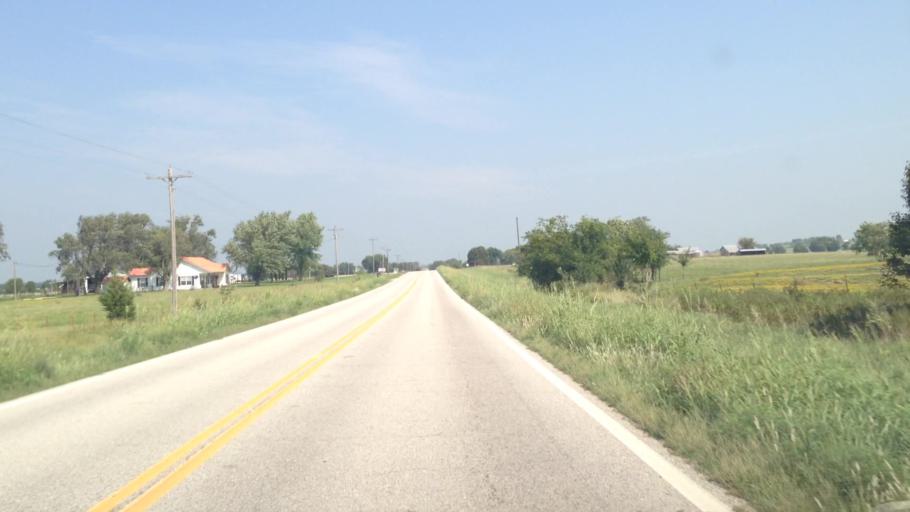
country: US
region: Oklahoma
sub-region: Craig County
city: Vinita
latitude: 36.8106
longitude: -95.1435
